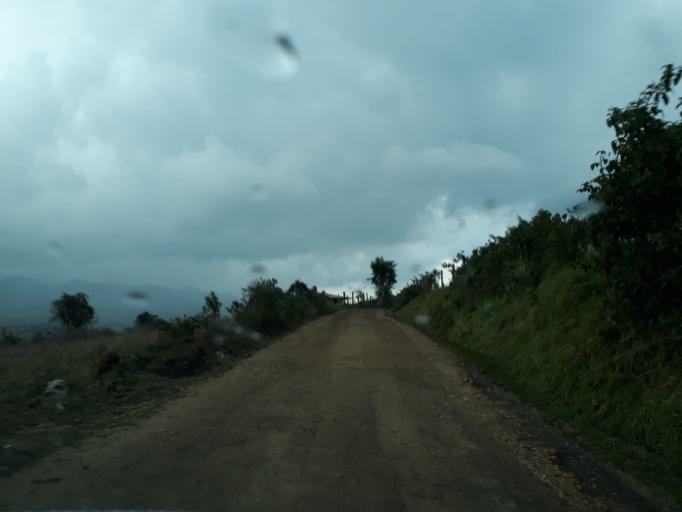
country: CO
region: Cundinamarca
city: Villapinzon
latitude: 5.2809
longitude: -73.6363
